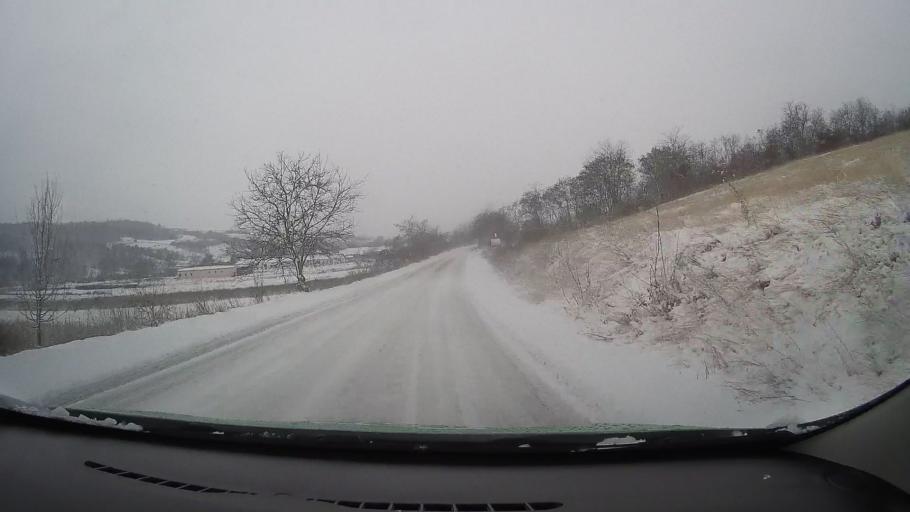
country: RO
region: Hunedoara
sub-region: Comuna Pestisu Mic
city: Pestisu Mic
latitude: 45.7984
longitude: 22.8923
